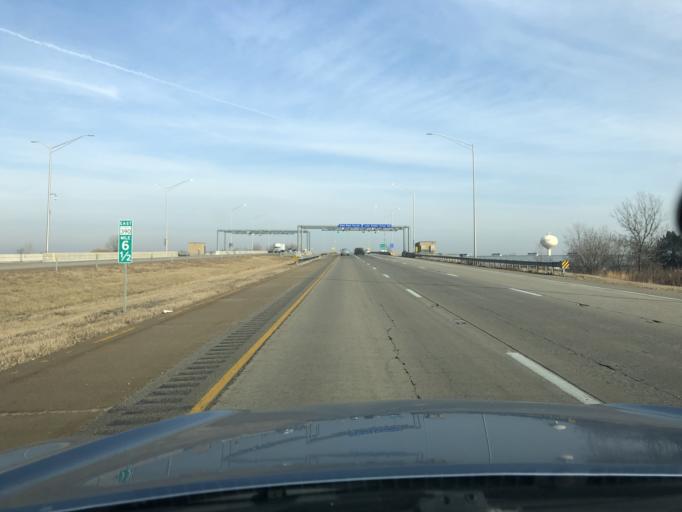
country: US
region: Illinois
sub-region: DuPage County
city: Hanover Park
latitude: 41.9860
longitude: -88.1313
